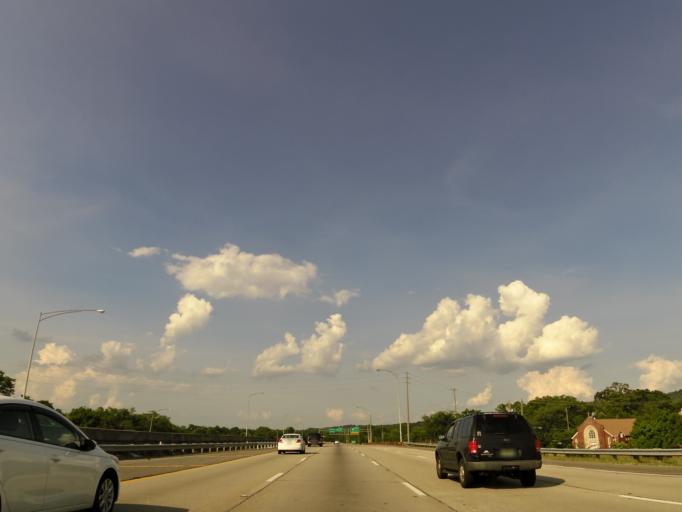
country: US
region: Alabama
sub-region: Jefferson County
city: Irondale
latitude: 33.5655
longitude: -86.7276
